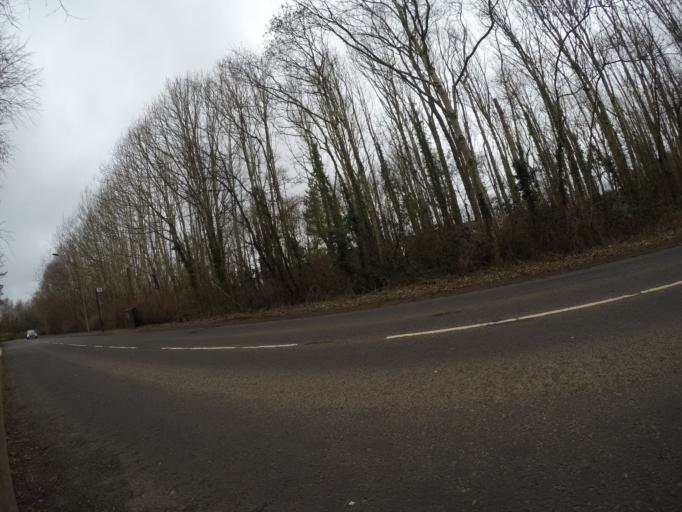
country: GB
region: Scotland
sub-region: North Ayrshire
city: Springside
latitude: 55.6313
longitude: -4.6253
